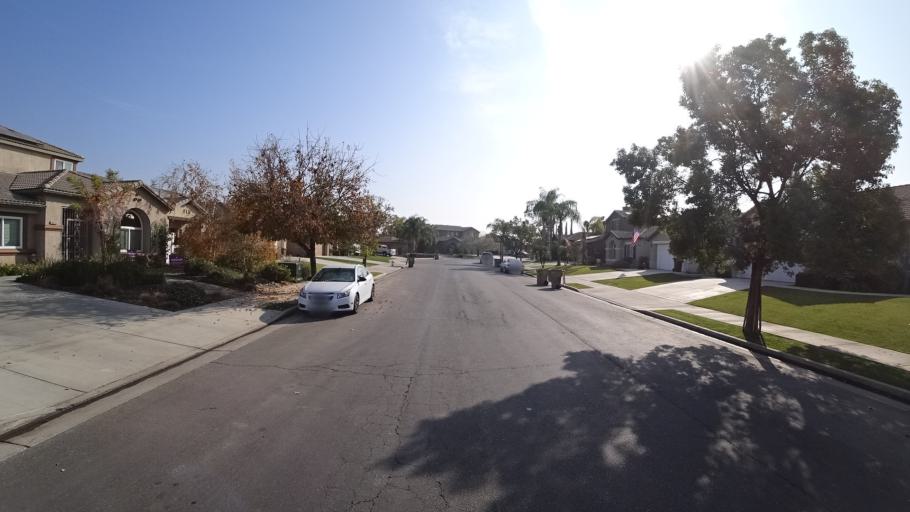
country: US
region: California
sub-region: Kern County
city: Greenacres
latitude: 35.4135
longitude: -119.1148
